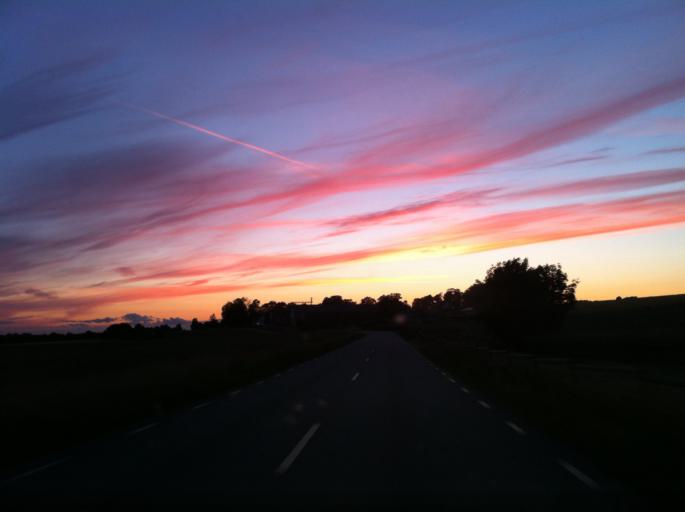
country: SE
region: Skane
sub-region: Sjobo Kommun
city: Sjoebo
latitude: 55.5959
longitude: 13.8065
